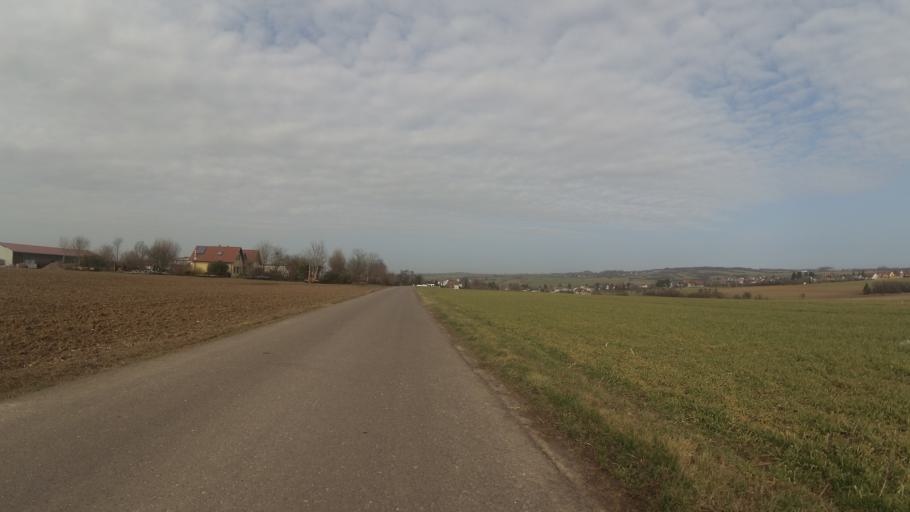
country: FR
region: Lorraine
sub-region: Departement de la Moselle
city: Merten
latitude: 49.2896
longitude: 6.6587
